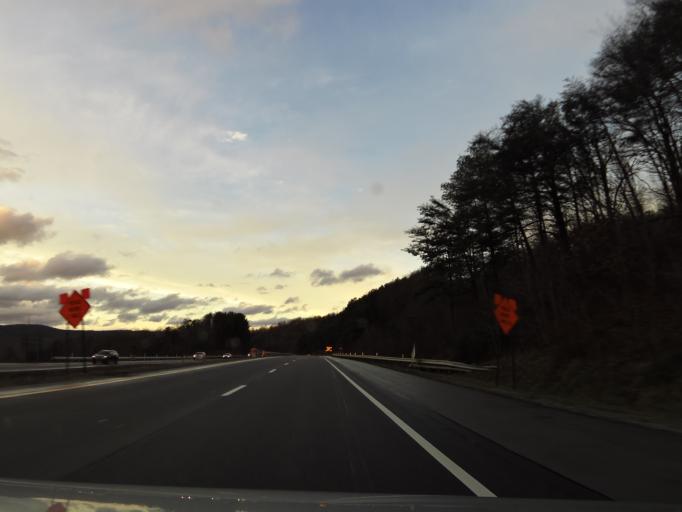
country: US
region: Tennessee
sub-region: Campbell County
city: Jacksboro
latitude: 36.3985
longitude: -84.2620
